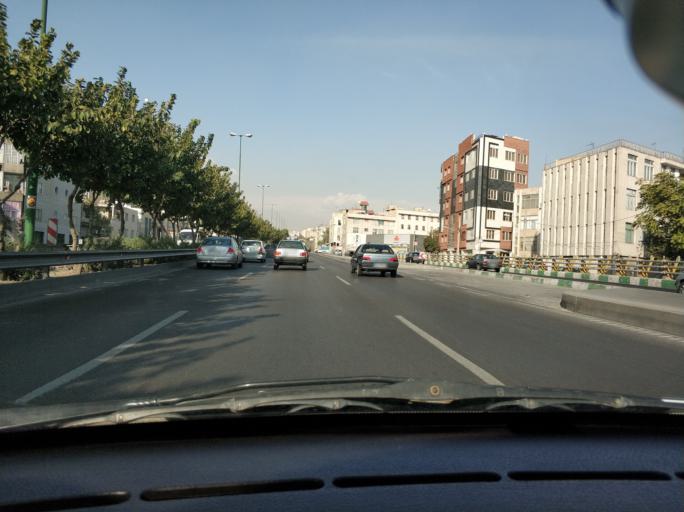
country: IR
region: Tehran
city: Tehran
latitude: 35.7165
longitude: 51.3557
